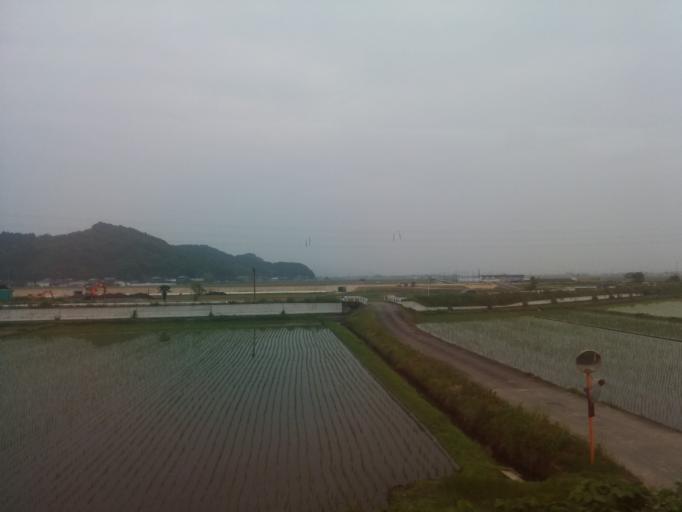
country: JP
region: Shiga Prefecture
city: Omihachiman
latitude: 35.1579
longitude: 136.1501
